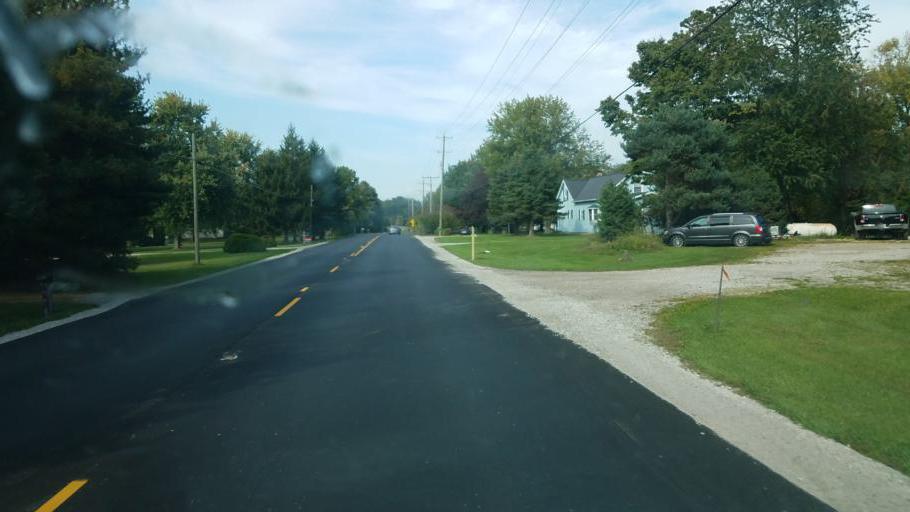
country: US
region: Ohio
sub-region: Franklin County
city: New Albany
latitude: 40.1009
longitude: -82.7792
